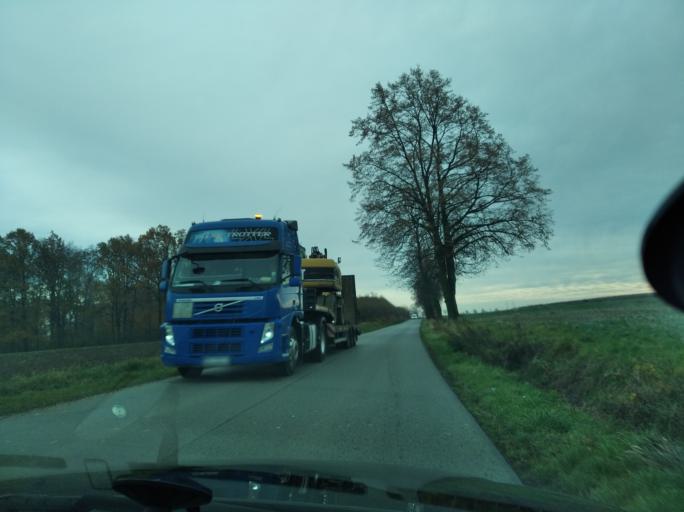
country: PL
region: Subcarpathian Voivodeship
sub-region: Powiat lancucki
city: Wysoka
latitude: 50.0282
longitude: 22.2468
